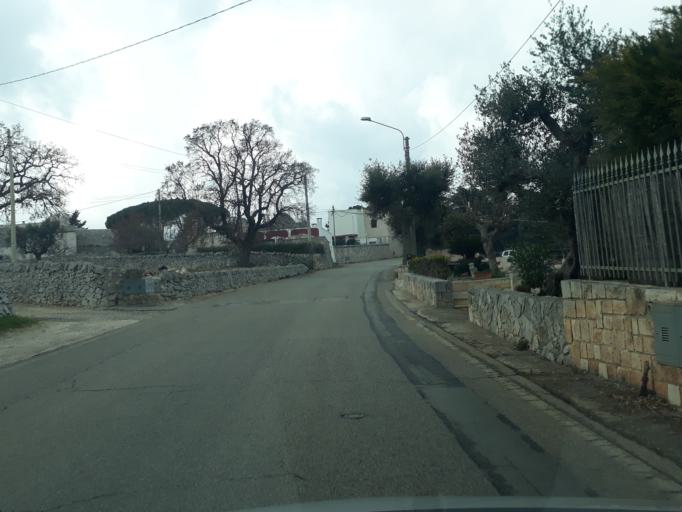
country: IT
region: Apulia
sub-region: Provincia di Brindisi
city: Lamie di Olimpie-Selva
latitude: 40.7908
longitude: 17.3203
